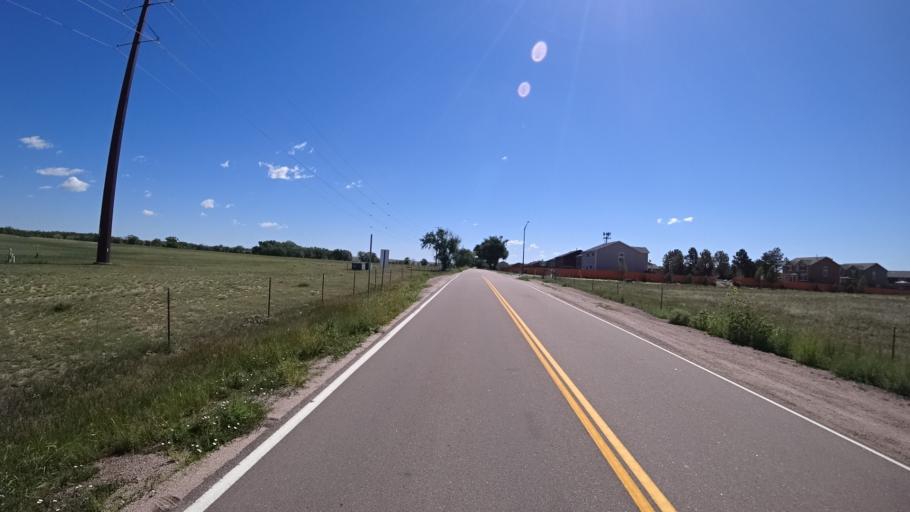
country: US
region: Colorado
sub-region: El Paso County
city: Security-Widefield
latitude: 38.7810
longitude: -104.6584
